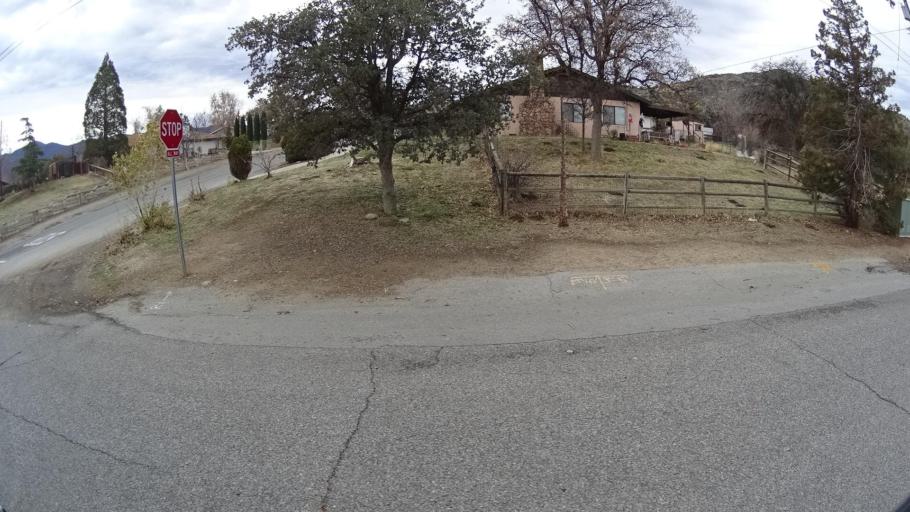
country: US
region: California
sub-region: Kern County
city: Golden Hills
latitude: 35.1387
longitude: -118.5055
